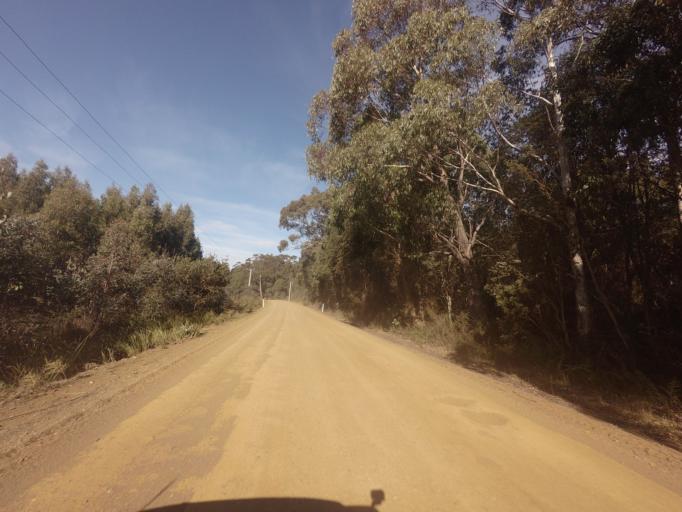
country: AU
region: Tasmania
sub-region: Sorell
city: Sorell
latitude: -42.5016
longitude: 147.5379
